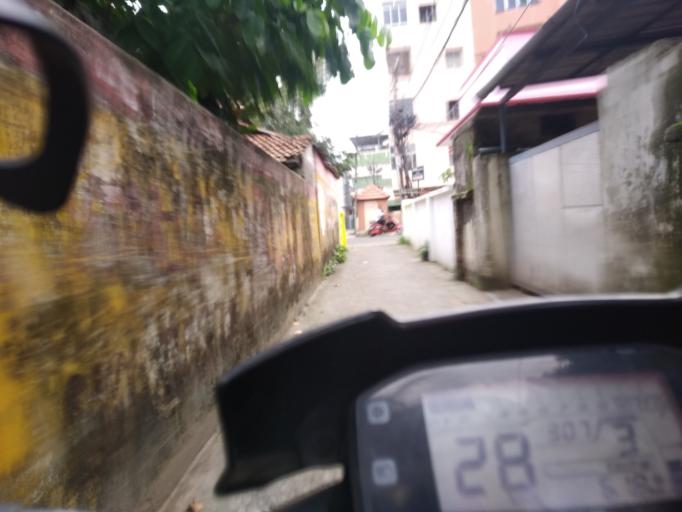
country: IN
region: Kerala
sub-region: Ernakulam
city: Cochin
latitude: 9.9894
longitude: 76.2826
